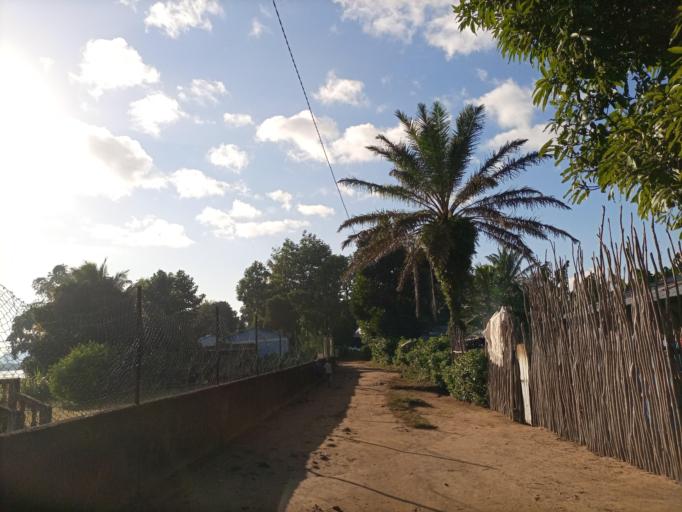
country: MG
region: Atsimo-Atsinanana
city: Vangaindrano
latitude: -23.3468
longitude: 47.6111
